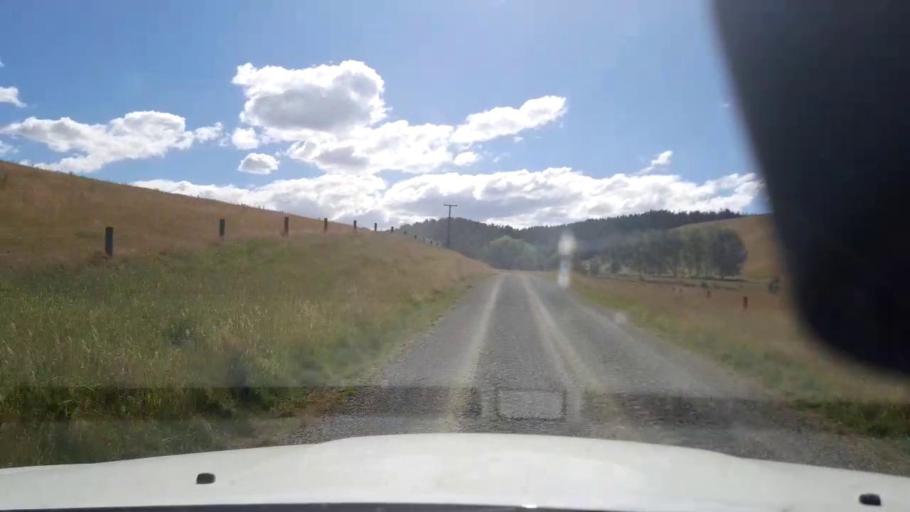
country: NZ
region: Canterbury
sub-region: Timaru District
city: Pleasant Point
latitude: -44.3118
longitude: 170.9147
